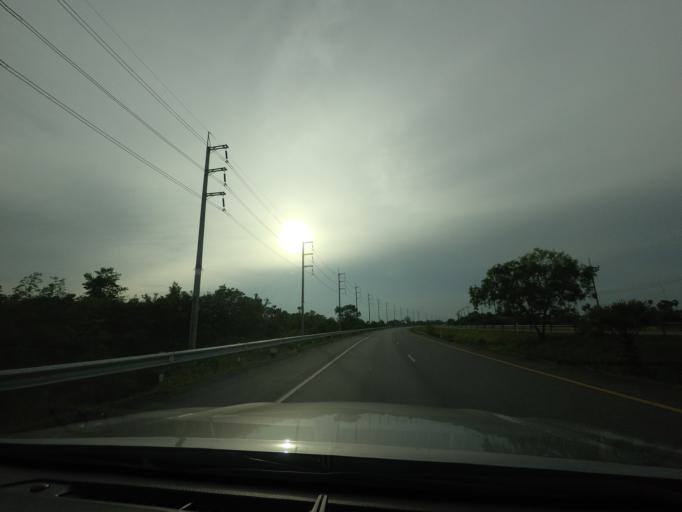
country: TH
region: Nakhon Si Thammarat
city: Hua Sai
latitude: 7.9982
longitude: 100.3081
